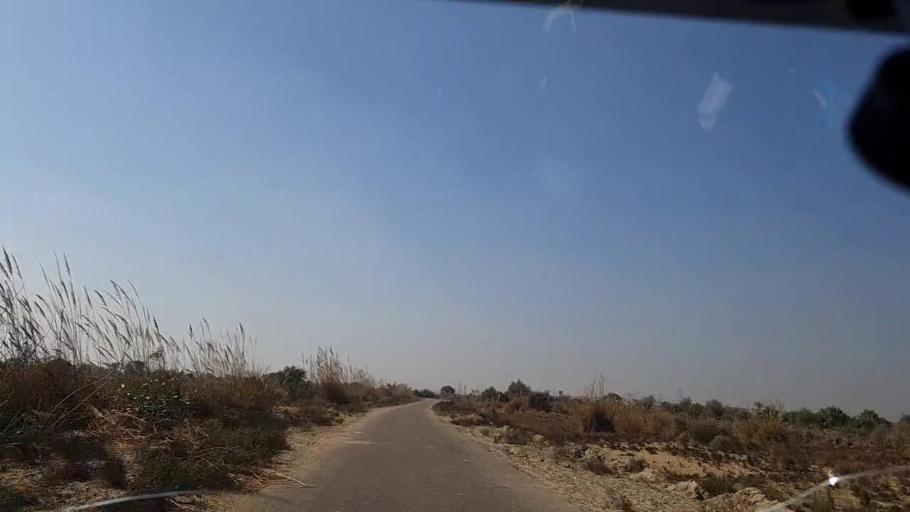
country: PK
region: Sindh
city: Khanpur
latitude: 27.5666
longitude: 69.3838
